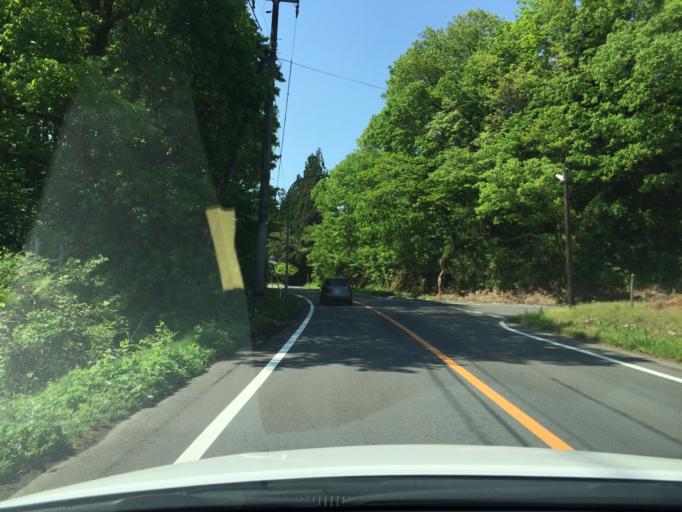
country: JP
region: Niigata
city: Muramatsu
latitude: 37.6562
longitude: 139.1369
